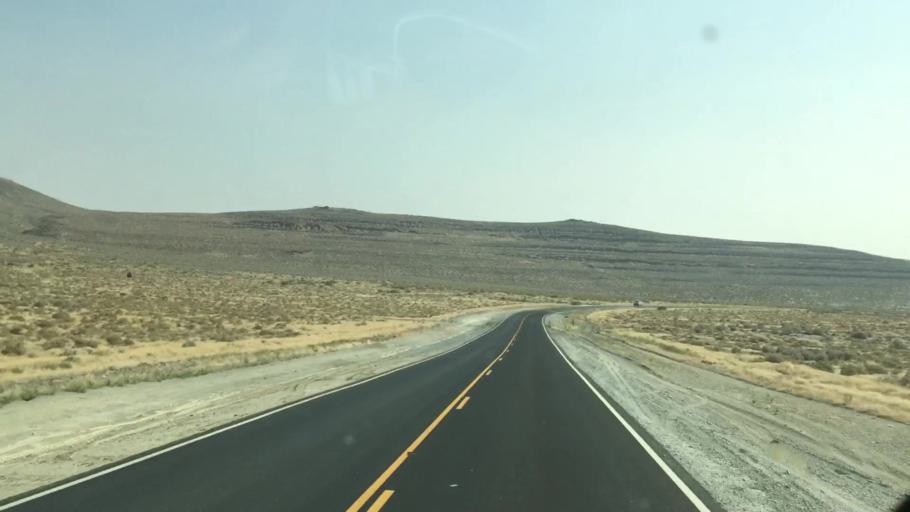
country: US
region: Nevada
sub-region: Pershing County
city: Lovelock
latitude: 40.7502
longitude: -119.2850
